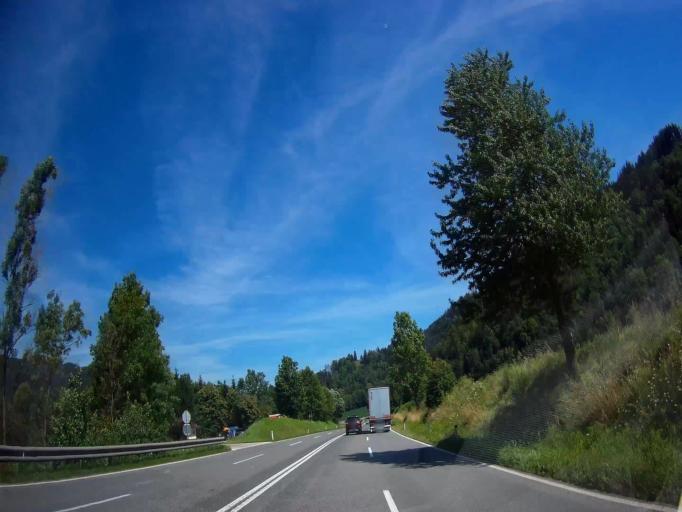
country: AT
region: Carinthia
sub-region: Politischer Bezirk Sankt Veit an der Glan
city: Micheldorf
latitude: 46.9100
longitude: 14.4370
